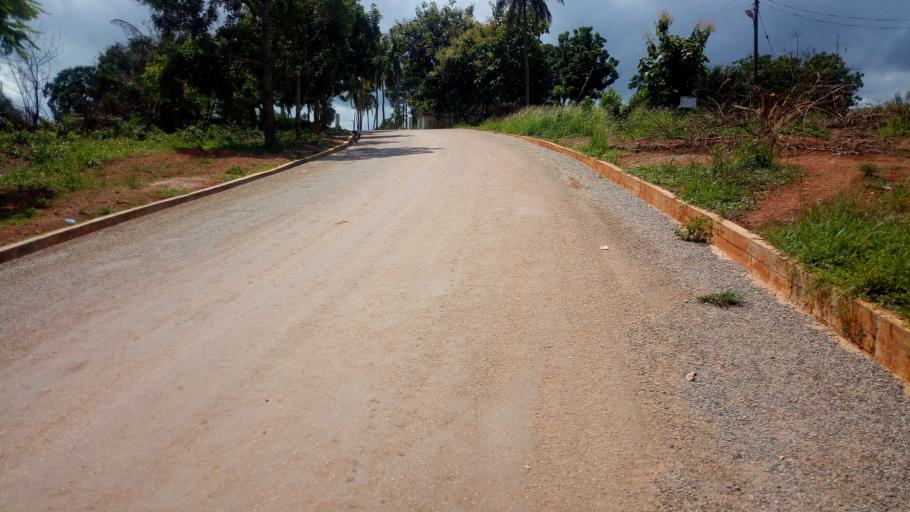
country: GH
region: Western
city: Sekondi-Takoradi
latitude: 4.9285
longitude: -1.7459
